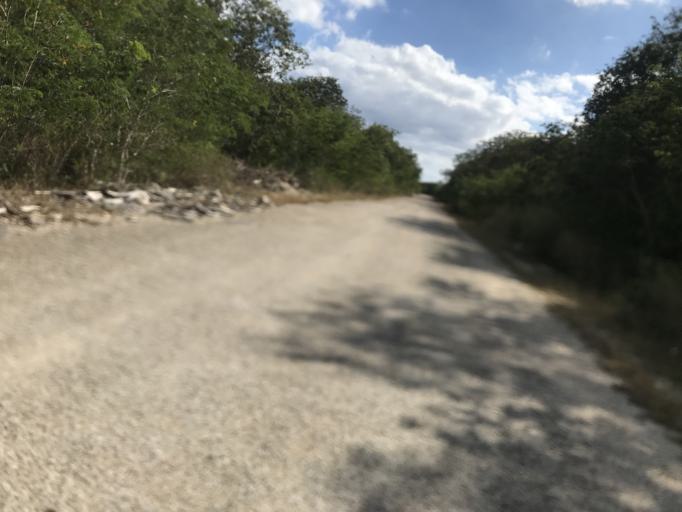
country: CU
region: Cienfuegos
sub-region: Municipio de Aguada de Pasajeros
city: Aguada de Pasajeros
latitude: 22.0744
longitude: -81.0364
